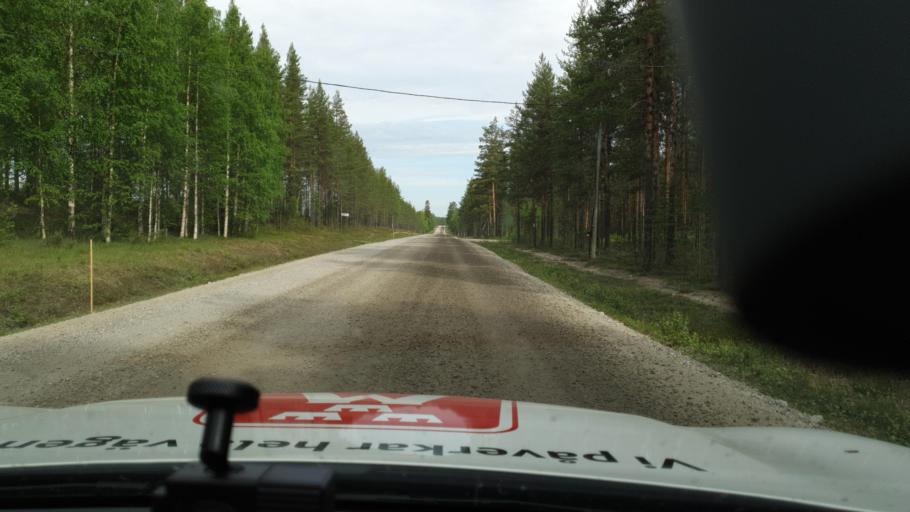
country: SE
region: Vaesterbotten
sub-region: Lycksele Kommun
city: Lycksele
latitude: 64.8320
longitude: 18.7819
